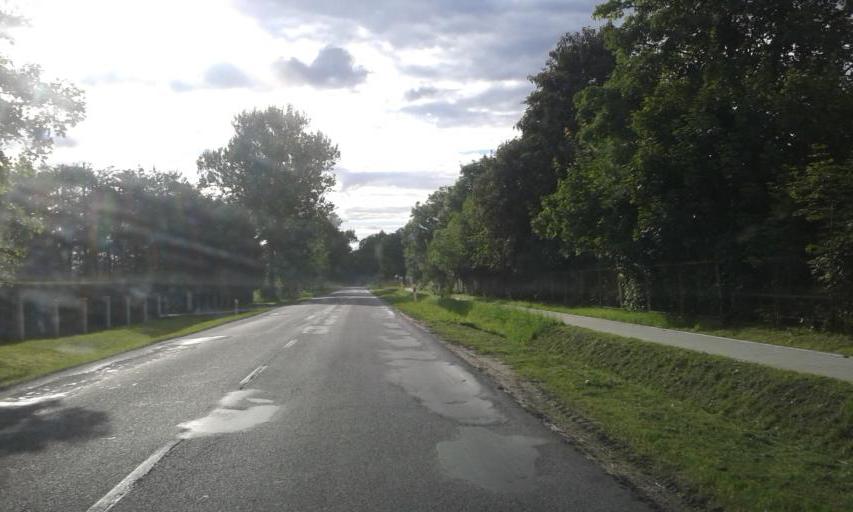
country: PL
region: West Pomeranian Voivodeship
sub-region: Powiat bialogardzki
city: Tychowo
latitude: 53.9262
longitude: 16.2502
